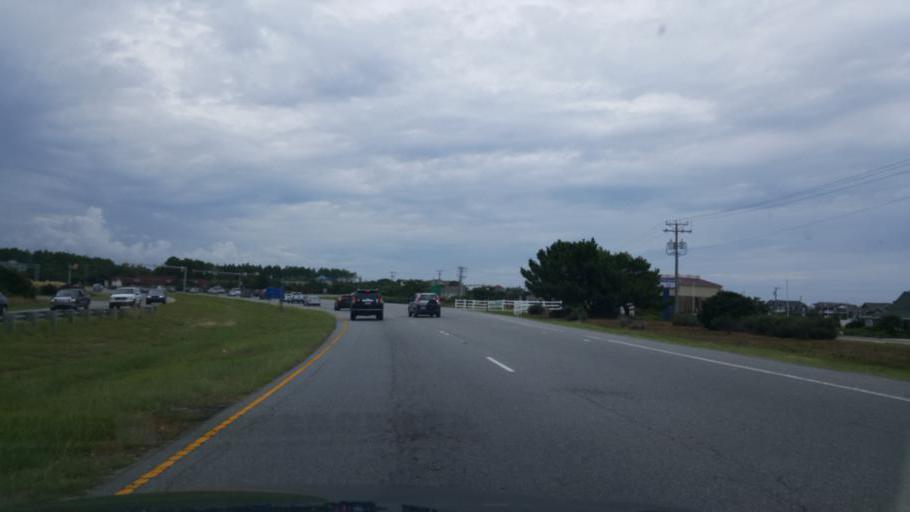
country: US
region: North Carolina
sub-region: Dare County
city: Kitty Hawk
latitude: 36.0980
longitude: -75.7128
